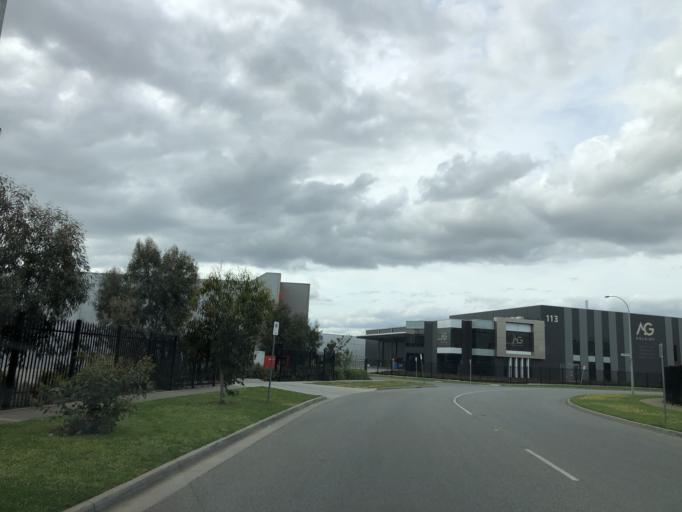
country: AU
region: Victoria
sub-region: Frankston
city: Carrum Downs
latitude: -38.0923
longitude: 145.1620
